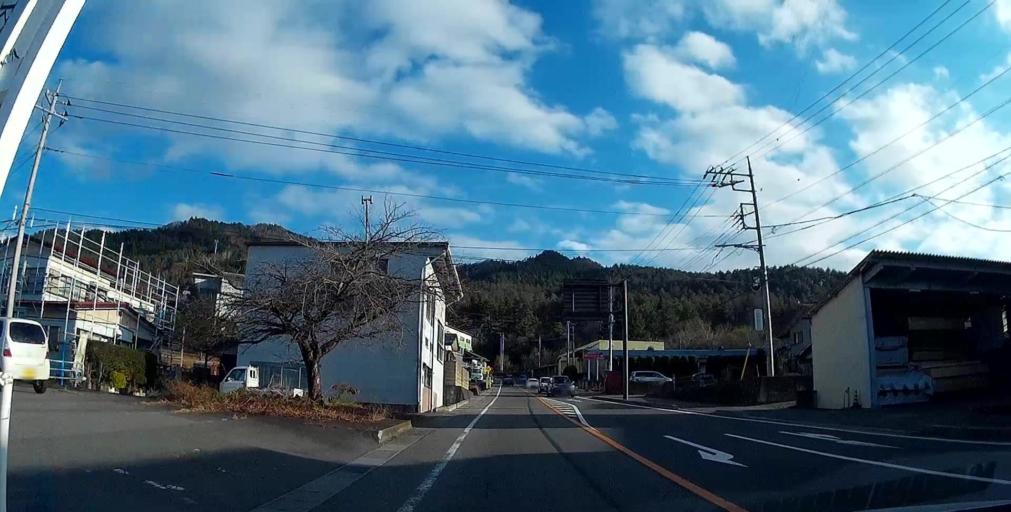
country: JP
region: Yamanashi
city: Fujikawaguchiko
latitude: 35.4776
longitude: 138.8161
